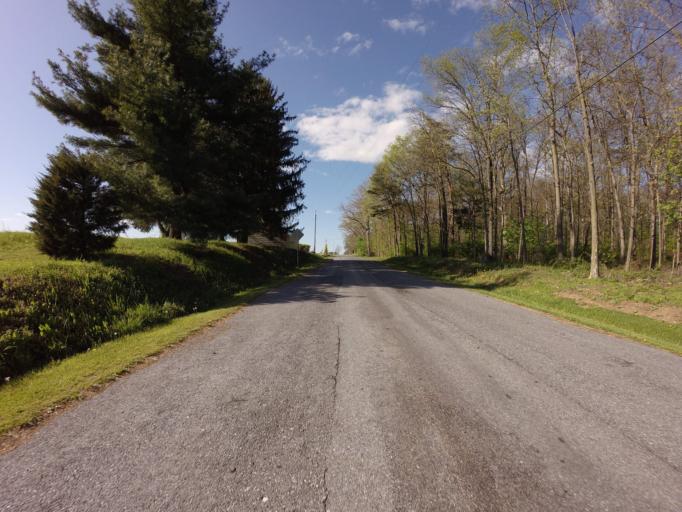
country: US
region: Maryland
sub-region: Frederick County
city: Emmitsburg
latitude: 39.6538
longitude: -77.2823
